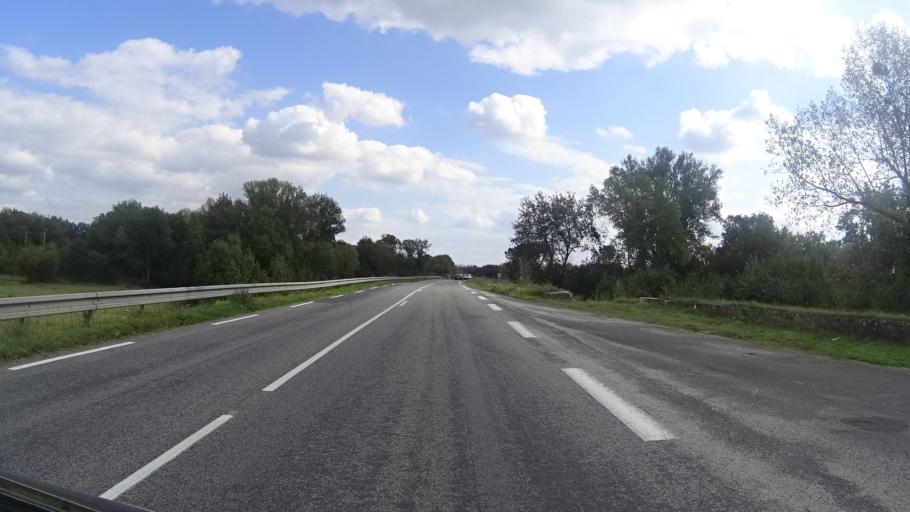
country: FR
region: Pays de la Loire
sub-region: Departement de Maine-et-Loire
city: Saint-Martin-de-la-Place
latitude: 47.3097
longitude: -0.1394
